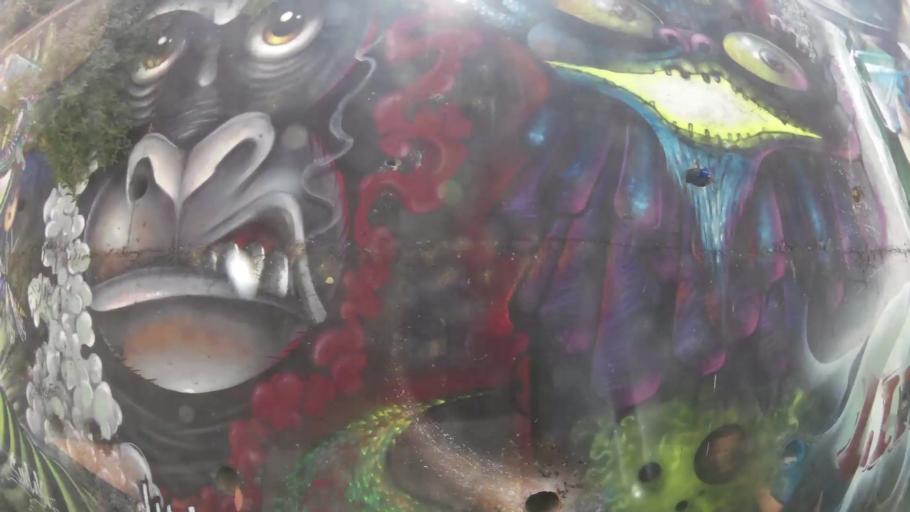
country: CL
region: Valparaiso
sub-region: Provincia de Valparaiso
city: Valparaiso
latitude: -33.0501
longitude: -71.5964
